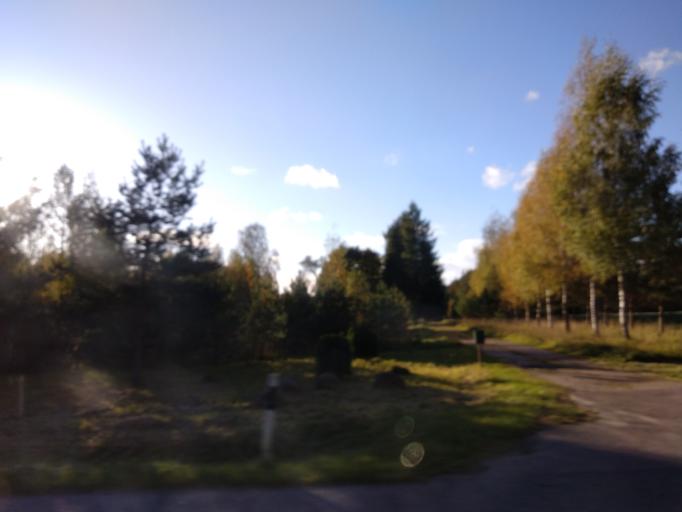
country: EE
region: Polvamaa
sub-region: Polva linn
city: Polva
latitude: 58.0319
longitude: 27.0661
